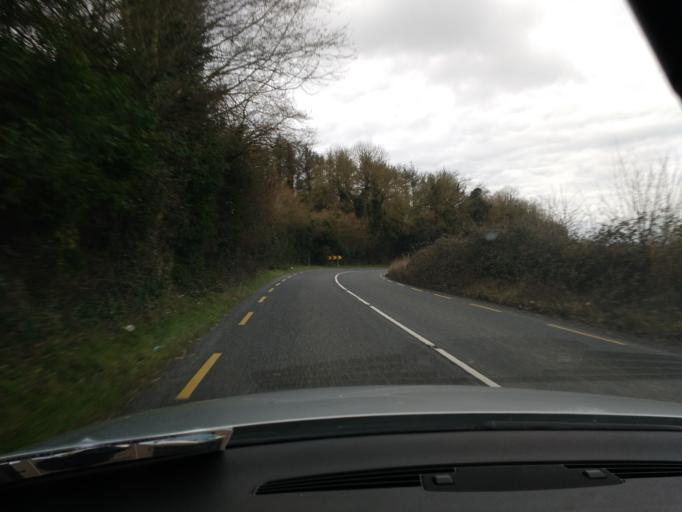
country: IE
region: Leinster
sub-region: Kilkenny
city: Kilkenny
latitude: 52.6940
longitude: -7.2886
